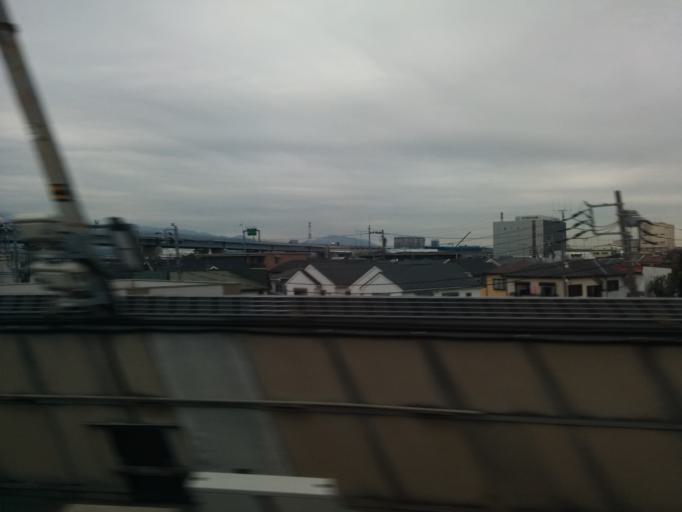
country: JP
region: Kanagawa
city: Atsugi
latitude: 35.3942
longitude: 139.3800
